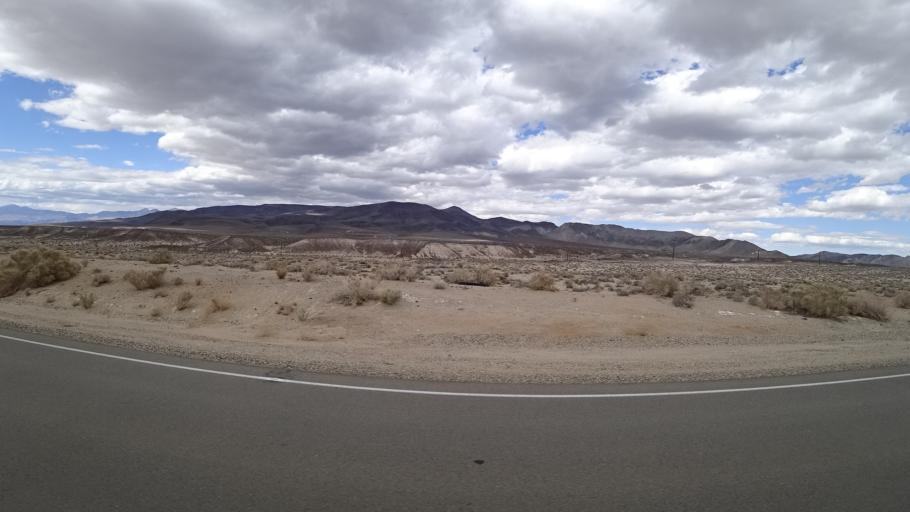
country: US
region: California
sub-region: Inyo County
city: Lone Pine
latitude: 36.3447
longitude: -117.7647
